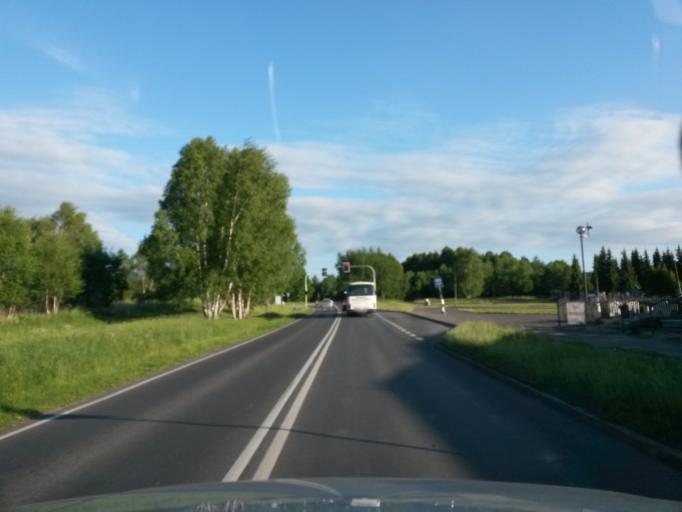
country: PL
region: Lower Silesian Voivodeship
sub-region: Jelenia Gora
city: Jelenia Gora
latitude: 50.8823
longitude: 15.7585
